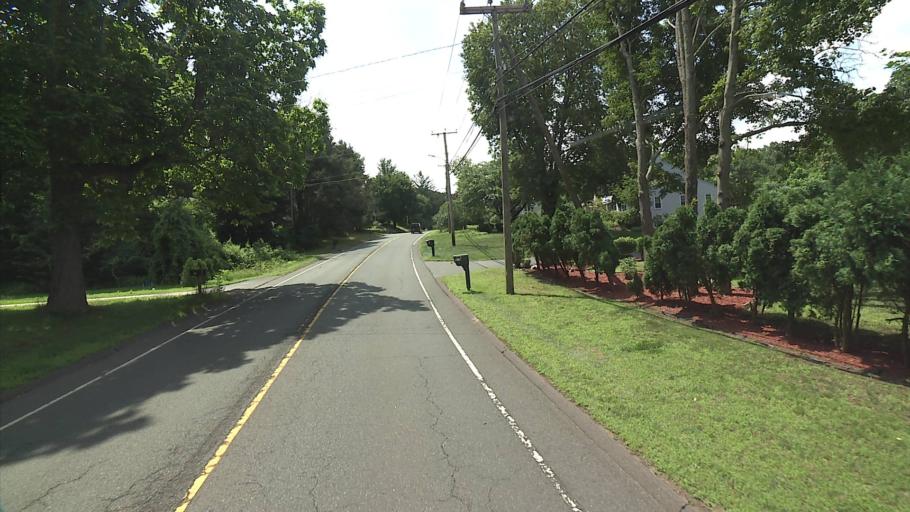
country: US
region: Connecticut
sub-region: Middlesex County
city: Cromwell
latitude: 41.6261
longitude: -72.6019
